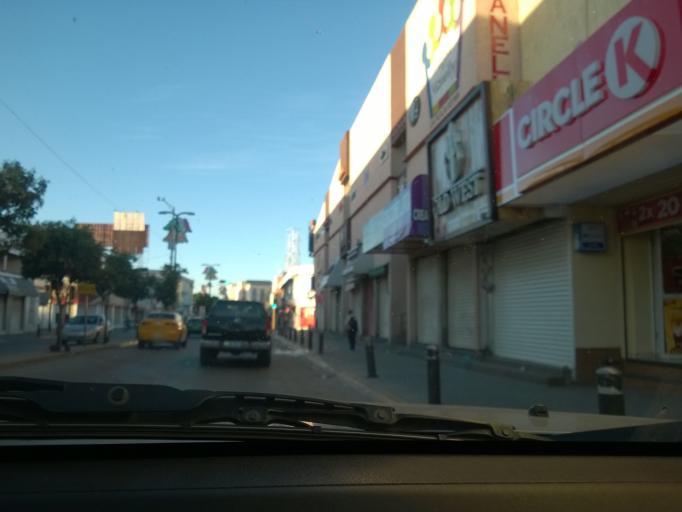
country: MX
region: Guanajuato
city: Leon
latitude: 21.1208
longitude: -101.6623
